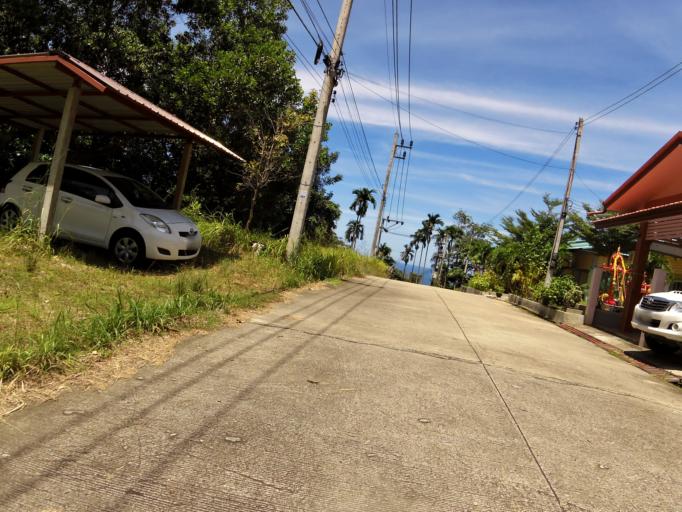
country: TH
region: Phuket
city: Ban Karon
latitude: 7.8489
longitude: 98.3074
